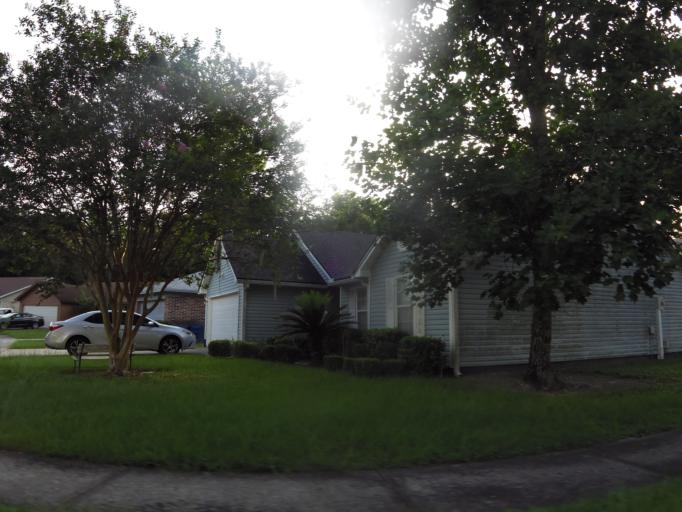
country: US
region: Florida
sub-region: Duval County
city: Jacksonville
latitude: 30.4428
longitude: -81.6839
